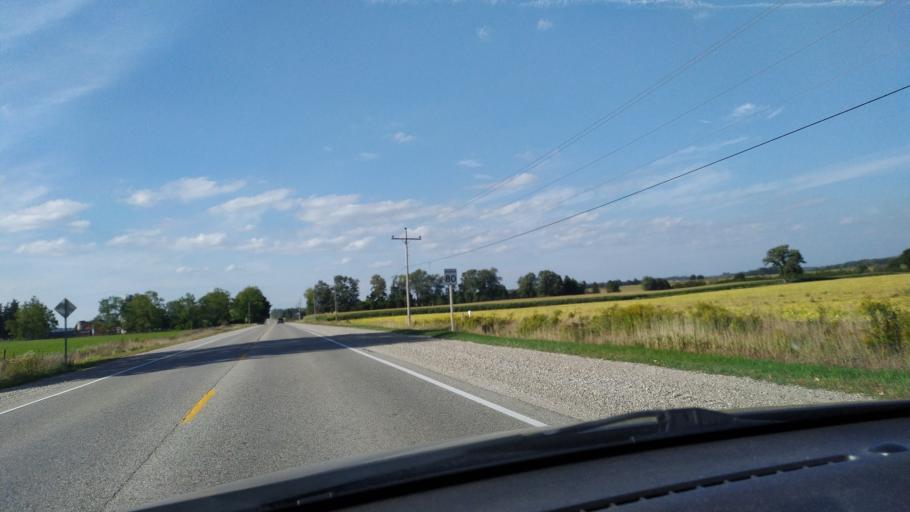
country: CA
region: Ontario
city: Ingersoll
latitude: 43.1244
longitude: -80.8856
